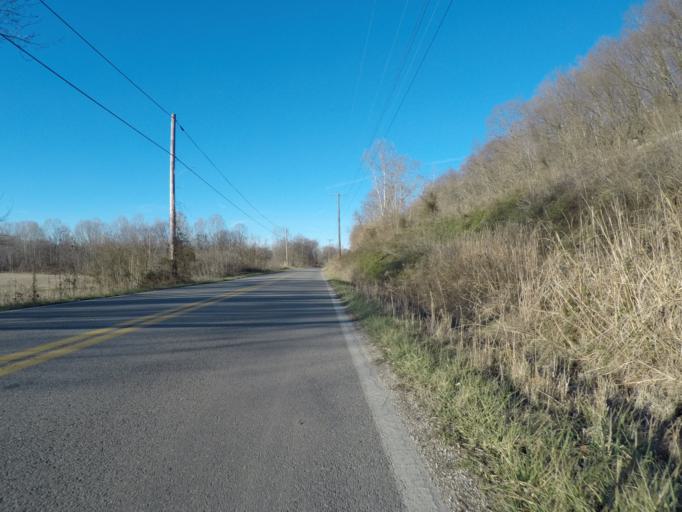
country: US
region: West Virginia
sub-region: Wayne County
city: Kenova
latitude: 38.3853
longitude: -82.5933
